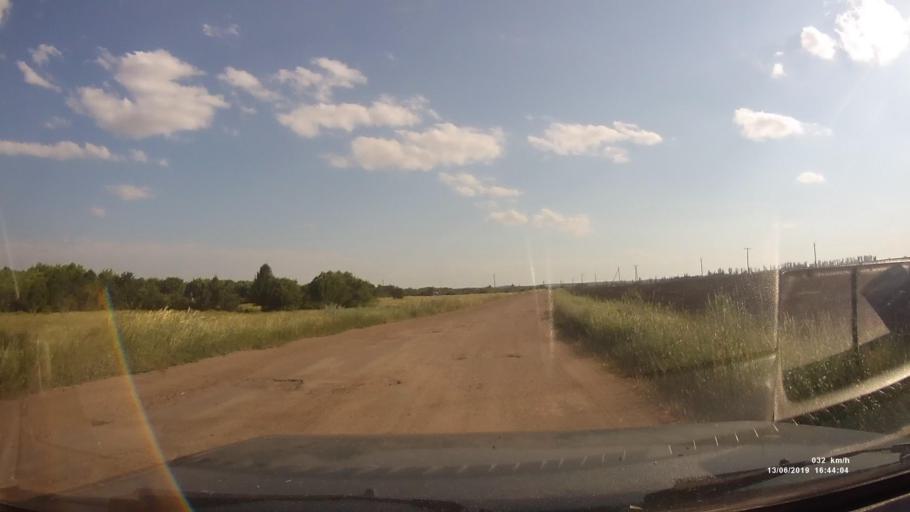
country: RU
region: Rostov
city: Kazanskaya
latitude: 49.9473
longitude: 41.4221
